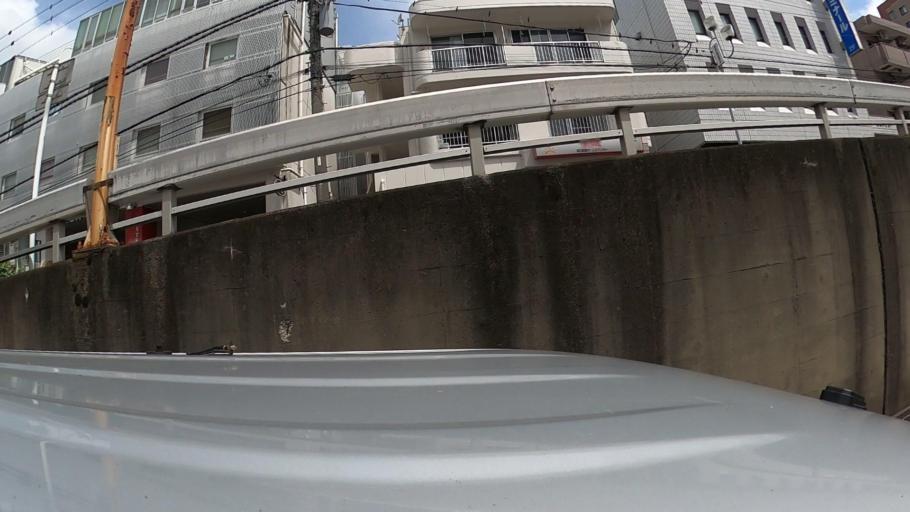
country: JP
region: Kanagawa
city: Fujisawa
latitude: 35.3977
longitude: 139.4654
